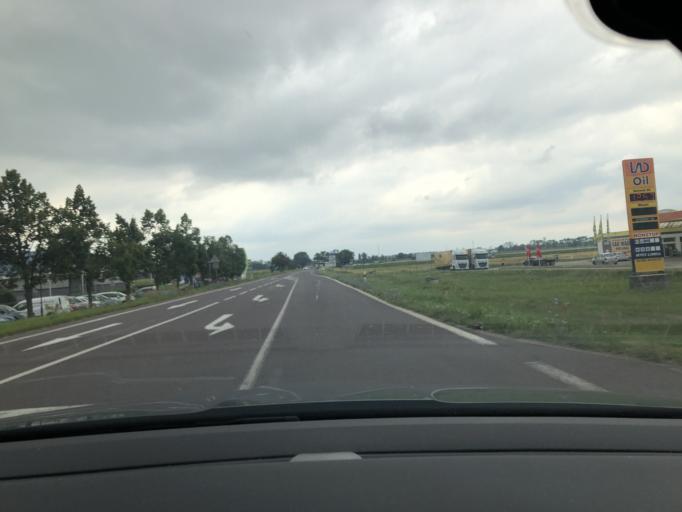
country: CZ
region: South Moravian
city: Hevlin
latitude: 48.7350
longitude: 16.3827
